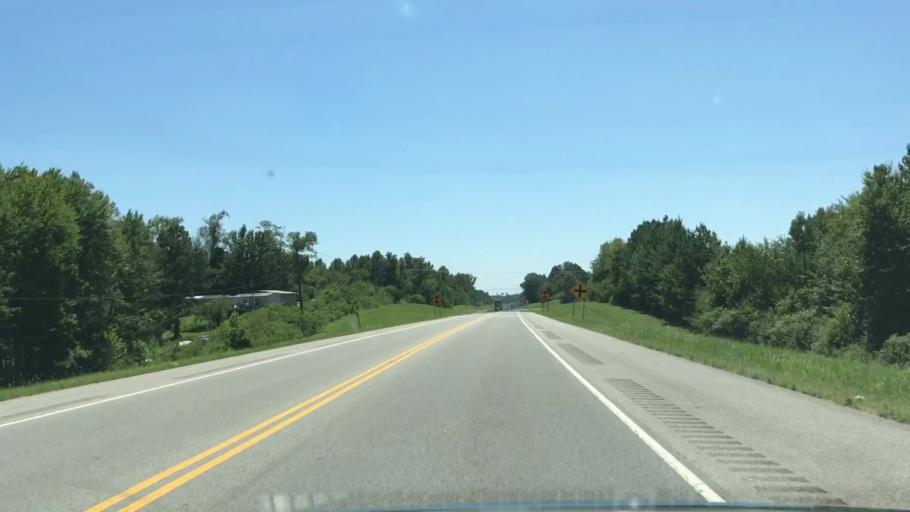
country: US
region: Tennessee
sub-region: Putnam County
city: Baxter
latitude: 36.1564
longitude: -85.6282
